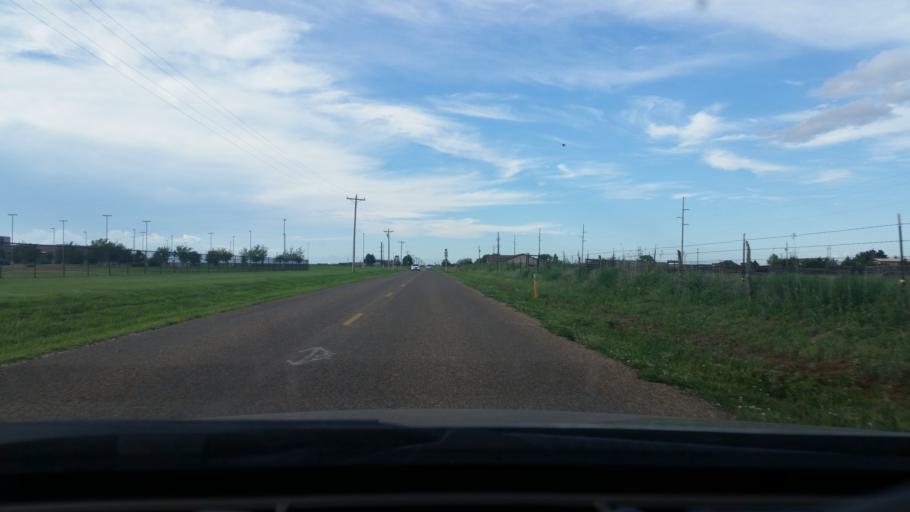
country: US
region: New Mexico
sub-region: Curry County
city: Clovis
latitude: 34.4500
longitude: -103.2140
